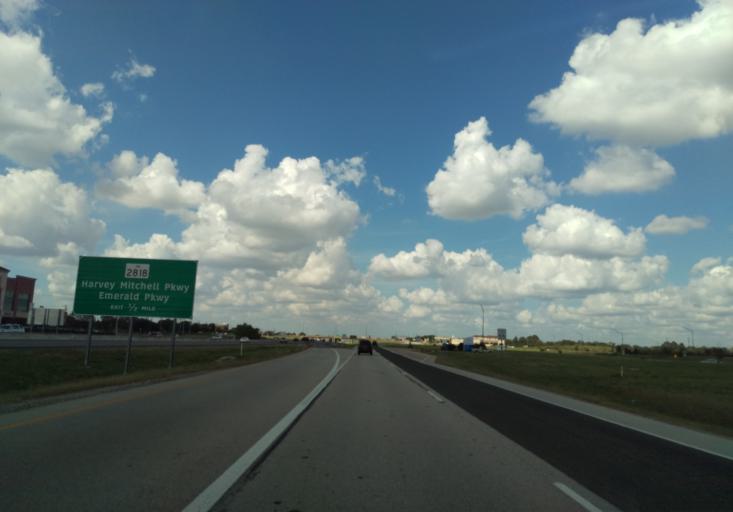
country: US
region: Texas
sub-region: Brazos County
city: College Station
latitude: 30.5790
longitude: -96.2810
